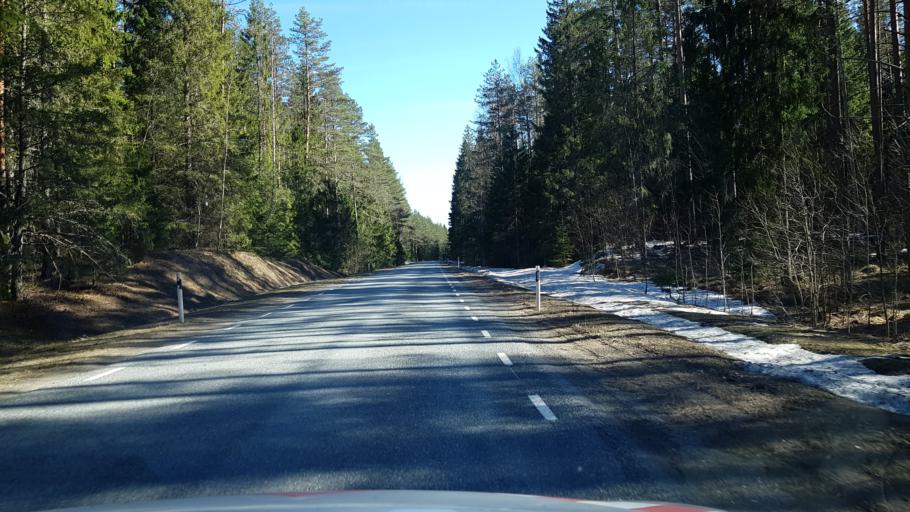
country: EE
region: Laeaene-Virumaa
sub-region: Vinni vald
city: Vinni
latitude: 59.2606
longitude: 26.6819
